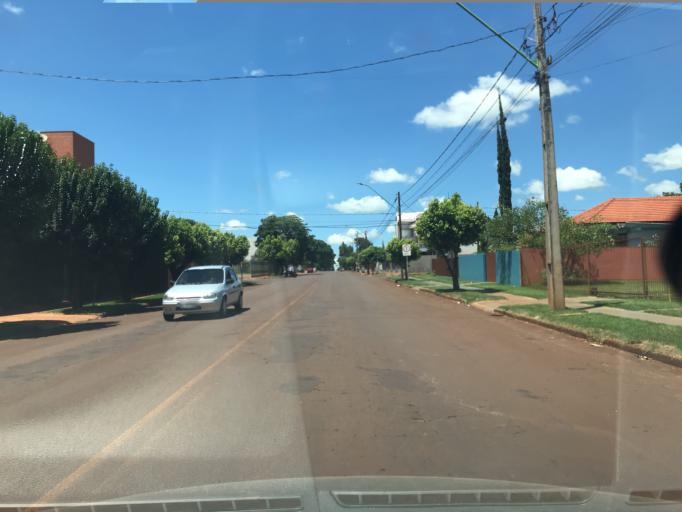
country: BR
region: Parana
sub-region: Palotina
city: Palotina
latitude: -24.2866
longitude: -53.8465
